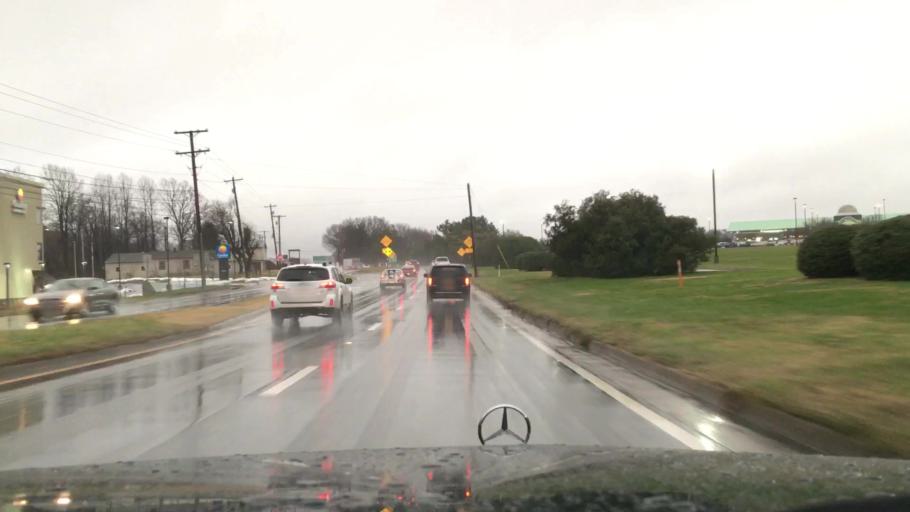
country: US
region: Virginia
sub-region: Campbell County
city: Timberlake
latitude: 37.3336
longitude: -79.1918
